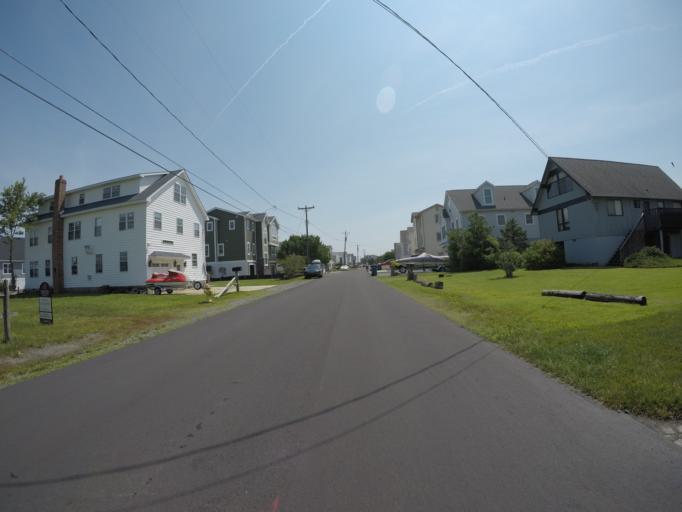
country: US
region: Delaware
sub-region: Sussex County
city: Bethany Beach
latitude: 38.5154
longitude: -75.0577
